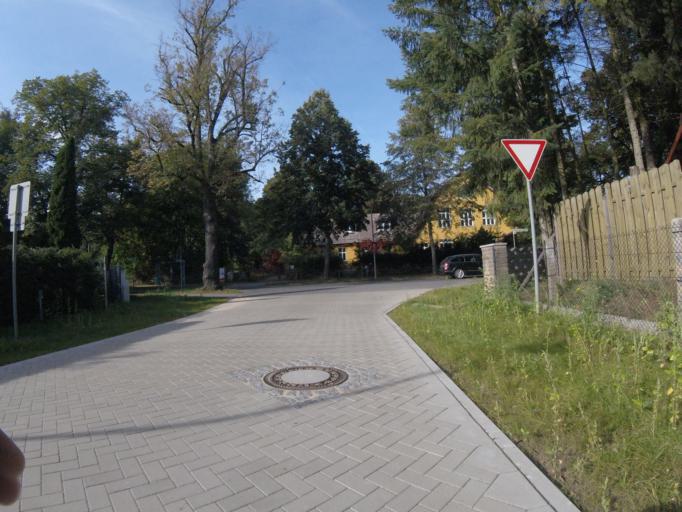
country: DE
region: Brandenburg
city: Konigs Wusterhausen
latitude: 52.2973
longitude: 13.6913
